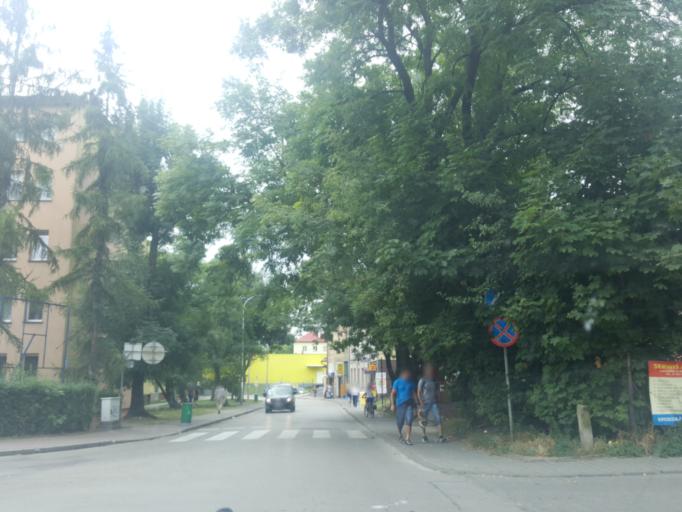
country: PL
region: Lesser Poland Voivodeship
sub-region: Powiat chrzanowski
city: Chrzanow
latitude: 50.1412
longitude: 19.4041
